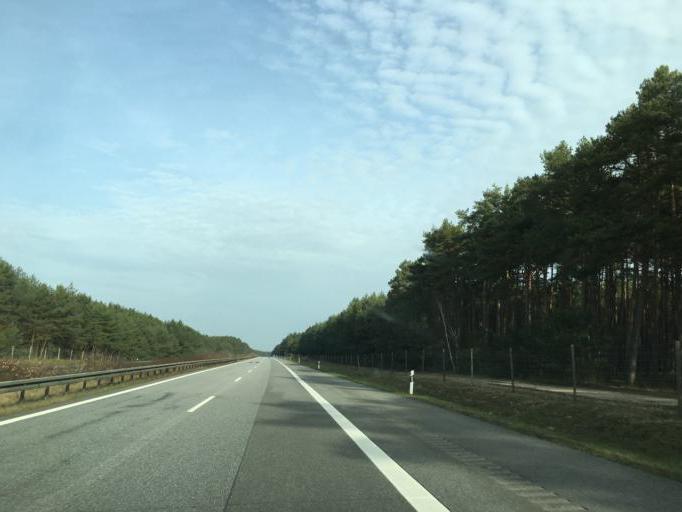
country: DE
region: Mecklenburg-Vorpommern
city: Malchow
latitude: 53.5392
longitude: 12.3434
